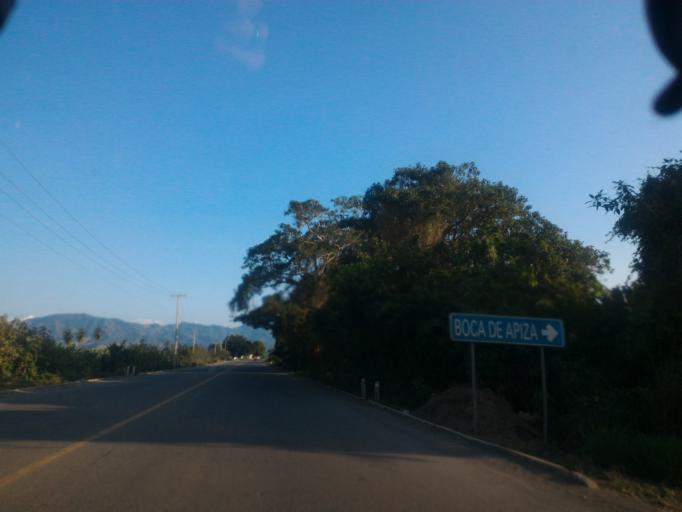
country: MX
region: Michoacan
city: Coahuayana Viejo
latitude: 18.7119
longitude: -103.7117
